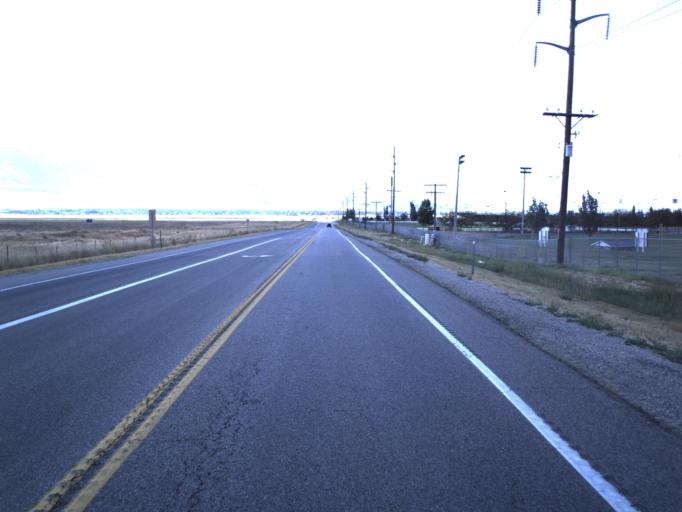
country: US
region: Utah
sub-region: Tooele County
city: Erda
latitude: 40.5672
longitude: -112.3680
